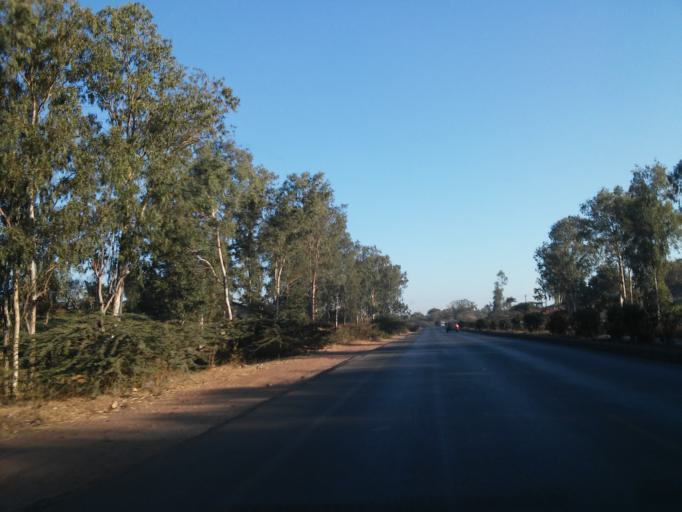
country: IN
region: Rajasthan
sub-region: Dungarpur
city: Dungarpur
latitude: 23.8439
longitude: 73.5250
